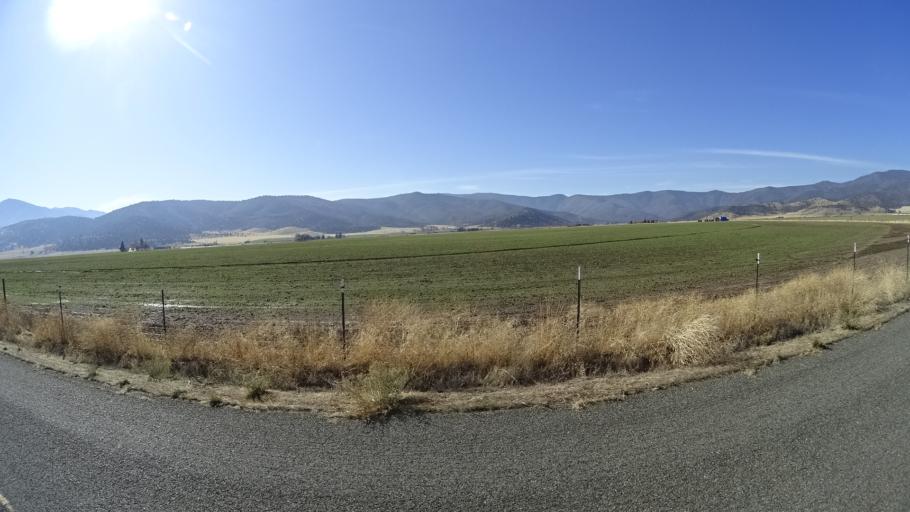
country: US
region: California
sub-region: Siskiyou County
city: Montague
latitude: 41.5448
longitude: -122.5393
